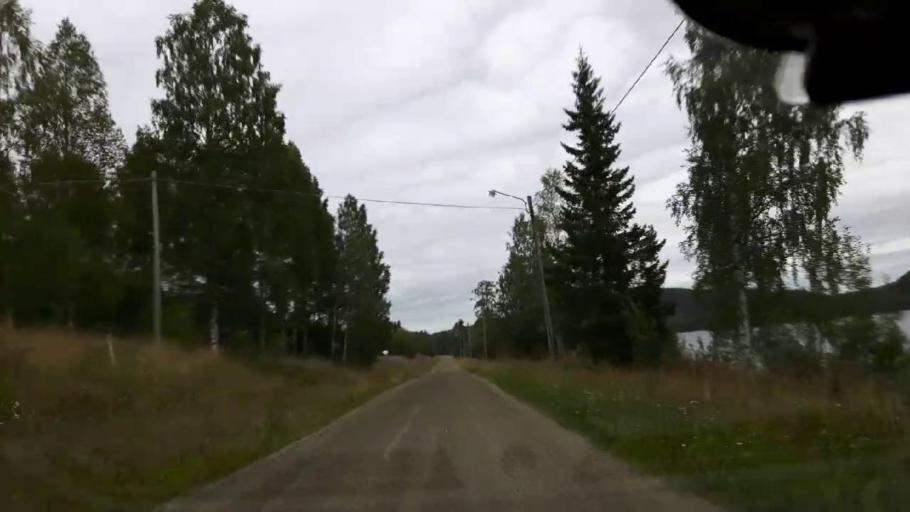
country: SE
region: Jaemtland
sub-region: Braecke Kommun
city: Braecke
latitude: 62.9972
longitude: 15.3819
